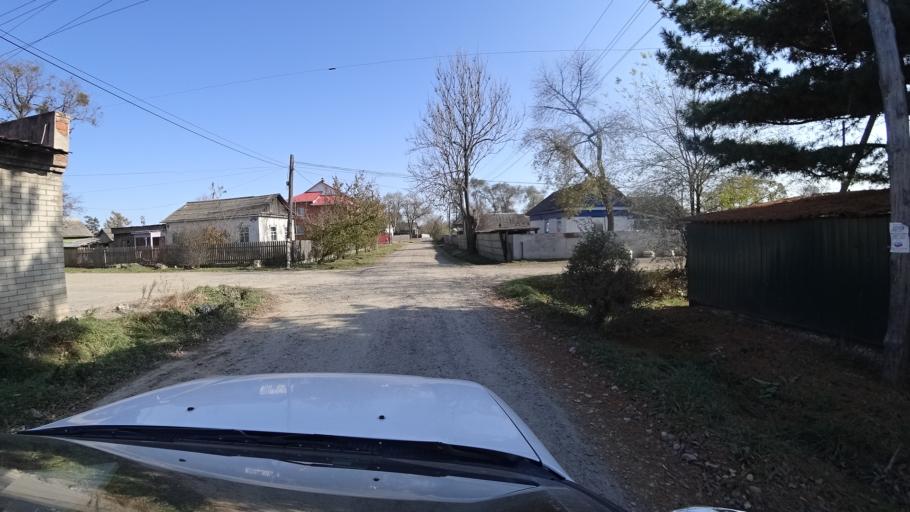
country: RU
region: Primorskiy
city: Dal'nerechensk
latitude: 45.9260
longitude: 133.7195
